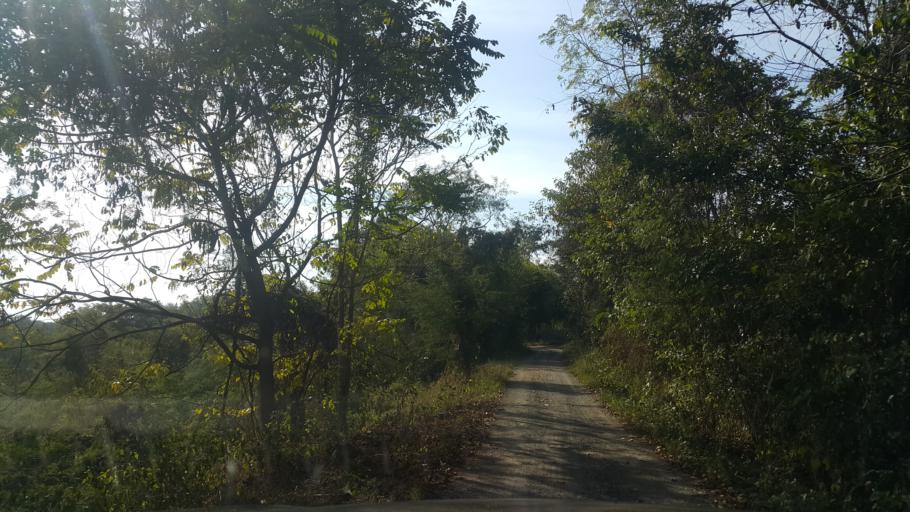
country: TH
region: Chiang Mai
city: Mae On
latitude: 18.7471
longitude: 99.2029
